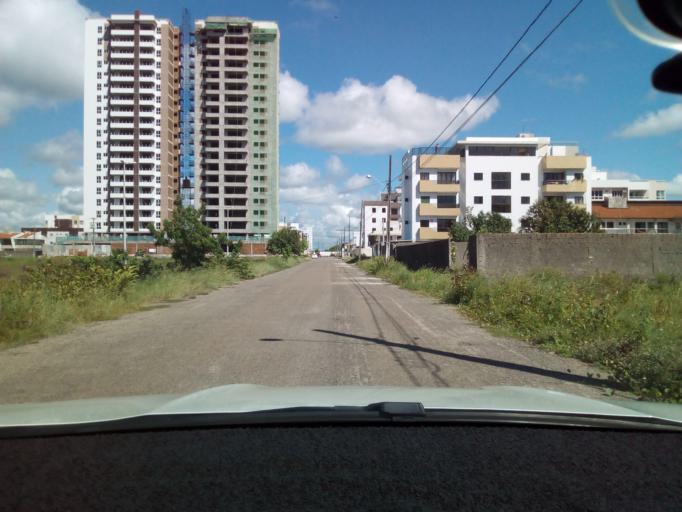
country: BR
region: Paraiba
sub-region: Joao Pessoa
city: Joao Pessoa
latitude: -7.0526
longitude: -34.8459
